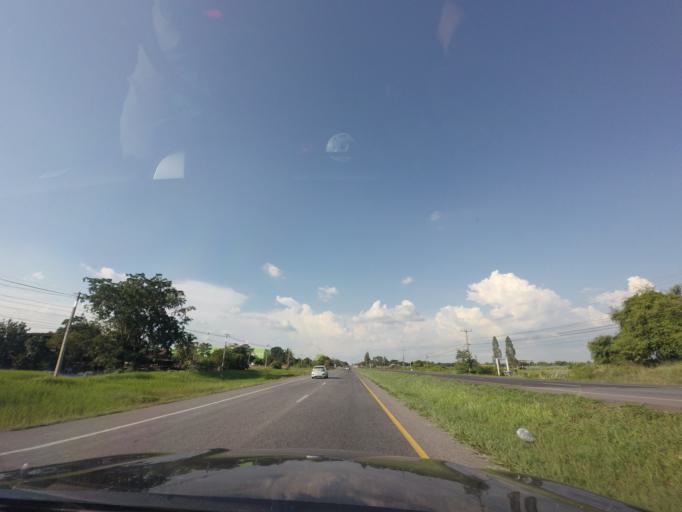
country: TH
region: Khon Kaen
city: Non Sila
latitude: 16.0019
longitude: 102.7022
